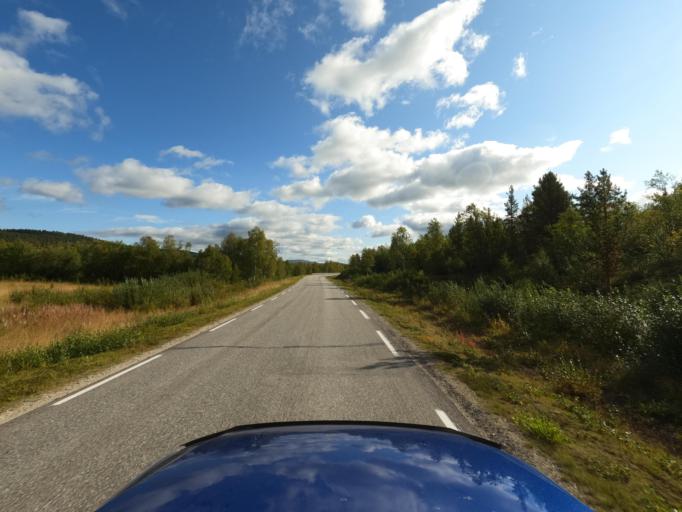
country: NO
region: Finnmark Fylke
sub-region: Karasjok
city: Karasjohka
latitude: 69.4477
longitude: 25.6149
